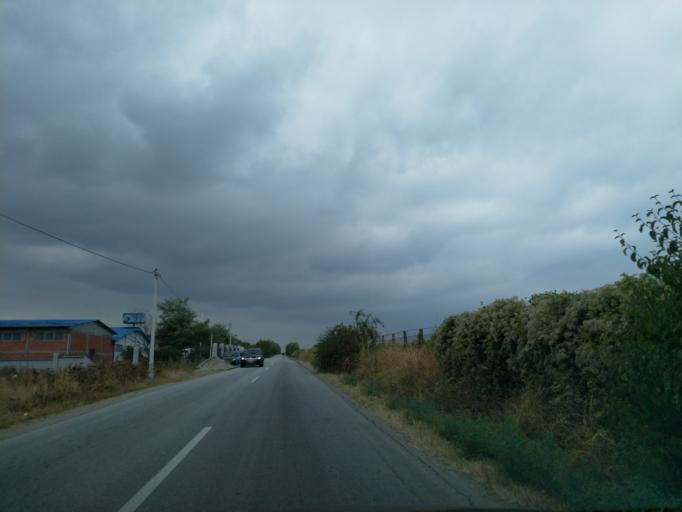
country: RS
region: Central Serbia
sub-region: Pomoravski Okrug
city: Jagodina
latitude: 43.9937
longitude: 21.2247
